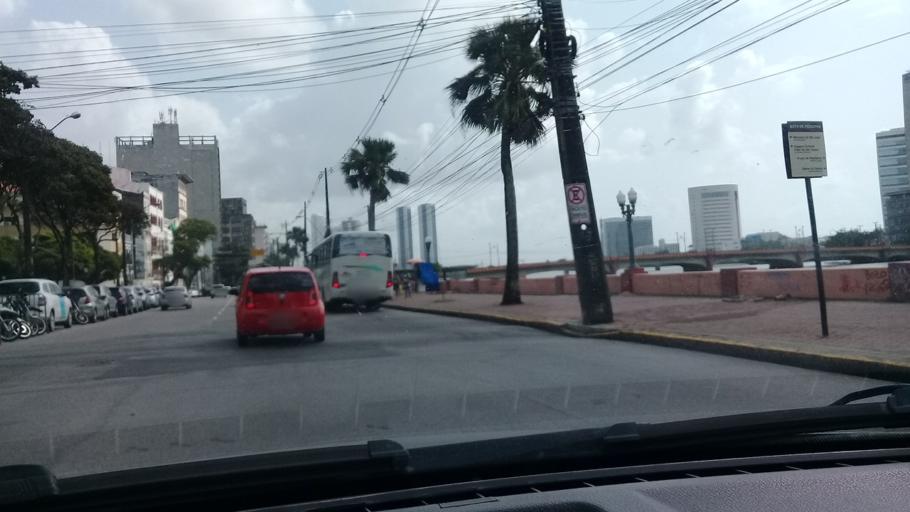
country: BR
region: Pernambuco
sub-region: Recife
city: Recife
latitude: -8.0661
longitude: -34.8761
